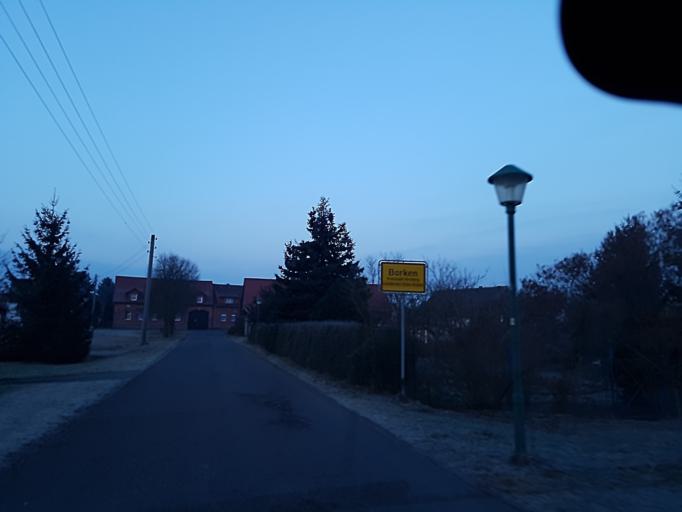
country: DE
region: Brandenburg
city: Herzberg
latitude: 51.7352
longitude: 13.2095
